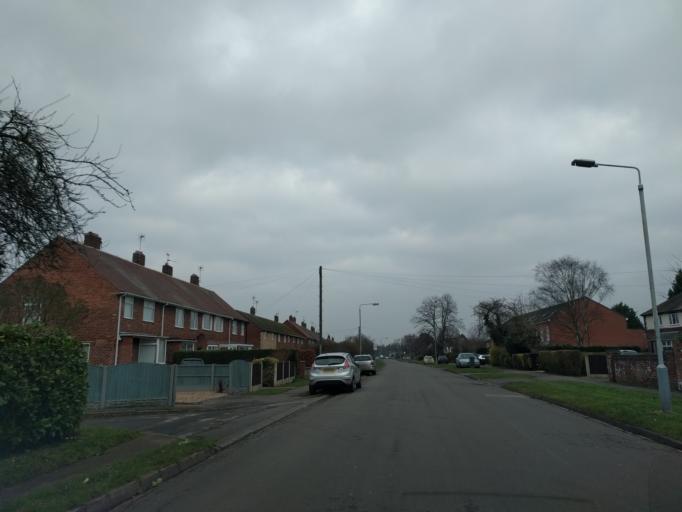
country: GB
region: England
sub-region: Nottinghamshire
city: Newark on Trent
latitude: 53.0892
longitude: -0.7975
